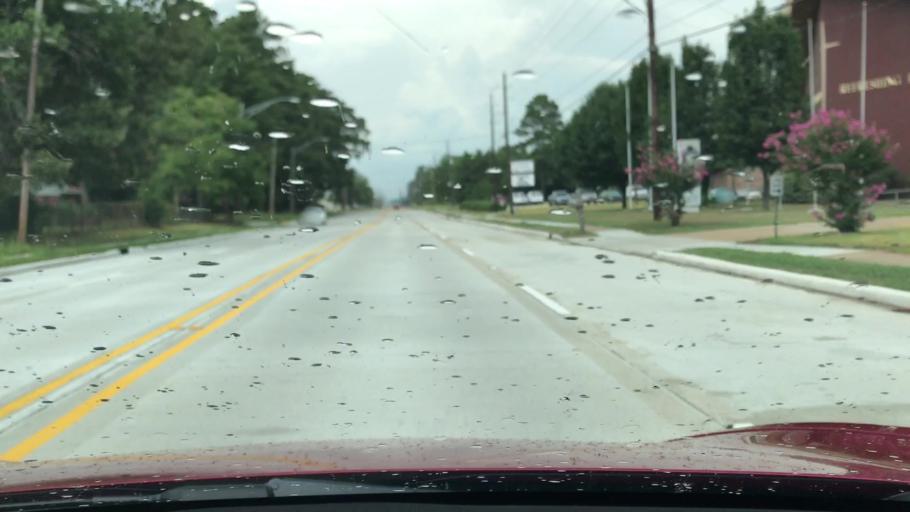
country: US
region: Louisiana
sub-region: Bossier Parish
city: Bossier City
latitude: 32.4071
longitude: -93.7632
